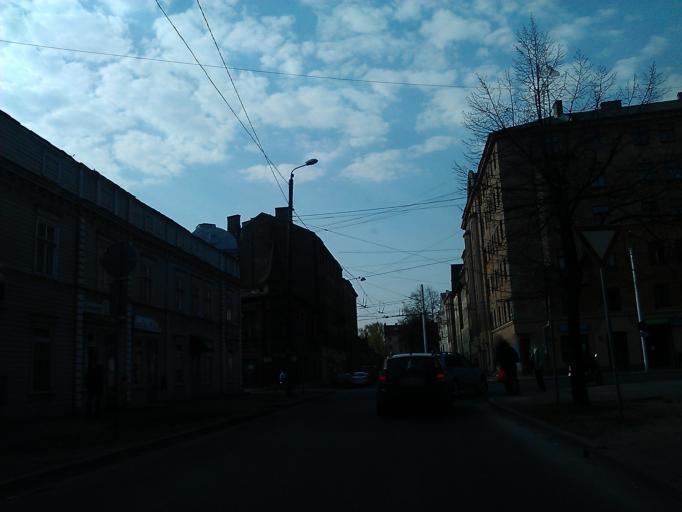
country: LV
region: Riga
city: Riga
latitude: 56.9534
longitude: 24.1470
